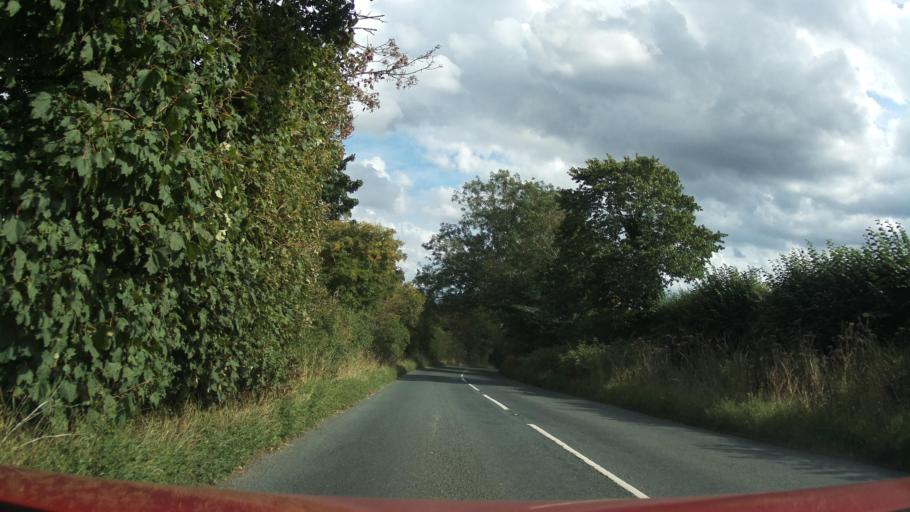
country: GB
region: England
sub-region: North Yorkshire
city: Bedale
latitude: 54.2069
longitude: -1.6023
